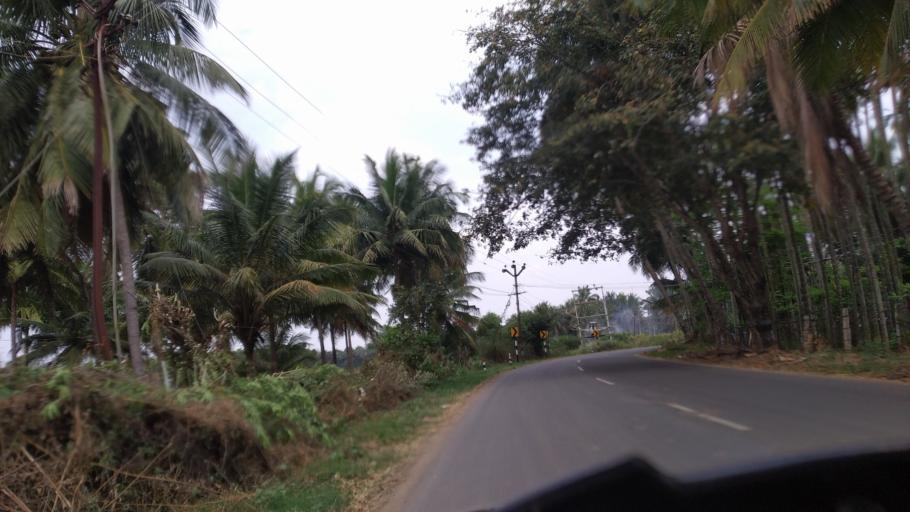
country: IN
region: Tamil Nadu
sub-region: Coimbatore
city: Perur
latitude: 10.9619
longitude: 76.7488
